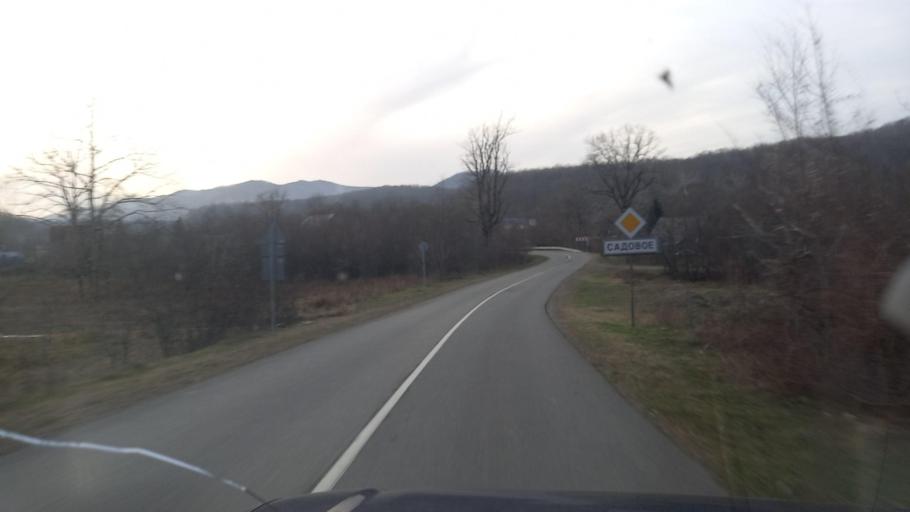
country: RU
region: Krasnodarskiy
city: Goryachiy Klyuch
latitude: 44.3878
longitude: 39.1772
